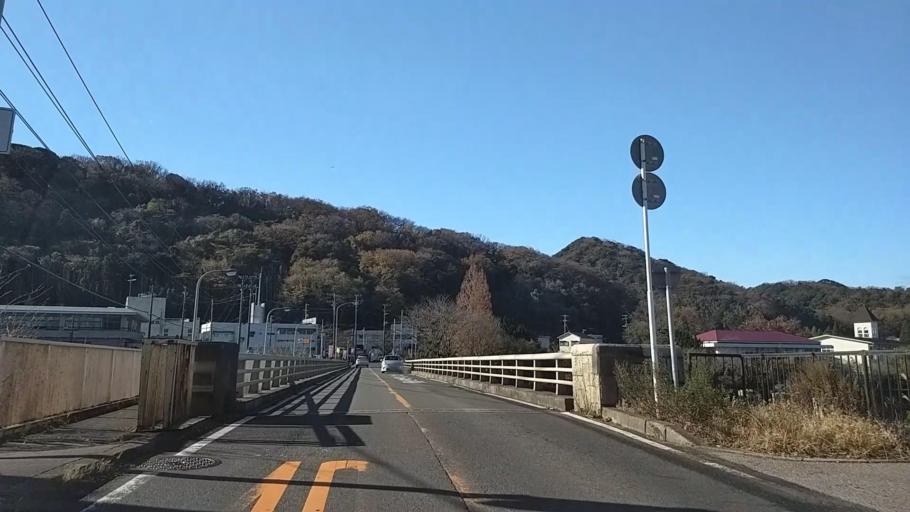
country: JP
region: Chiba
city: Futtsu
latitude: 35.2154
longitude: 139.8698
